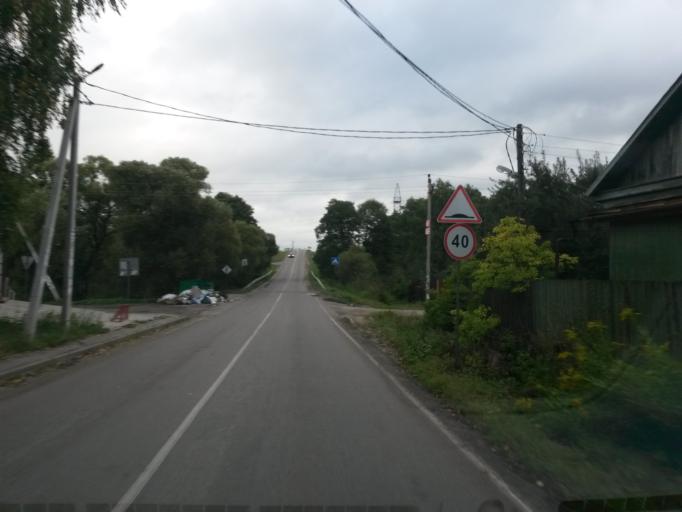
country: RU
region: Moskovskaya
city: Barybino
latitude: 55.2520
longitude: 37.8203
